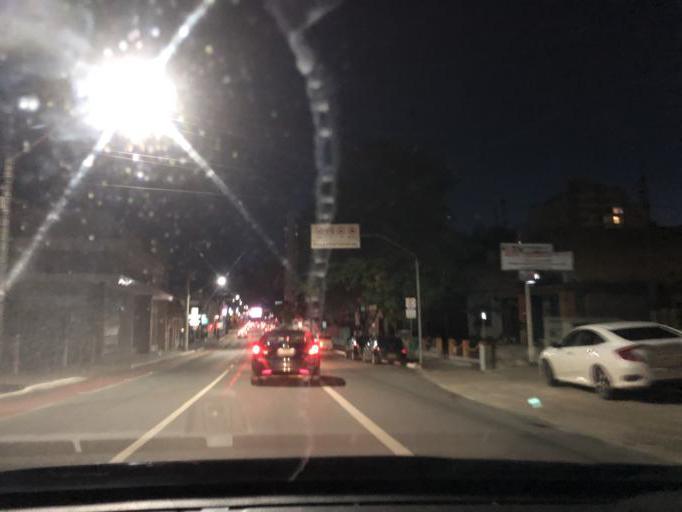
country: BR
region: Santa Catarina
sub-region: Jaragua Do Sul
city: Jaragua do Sul
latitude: -26.4816
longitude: -49.0843
